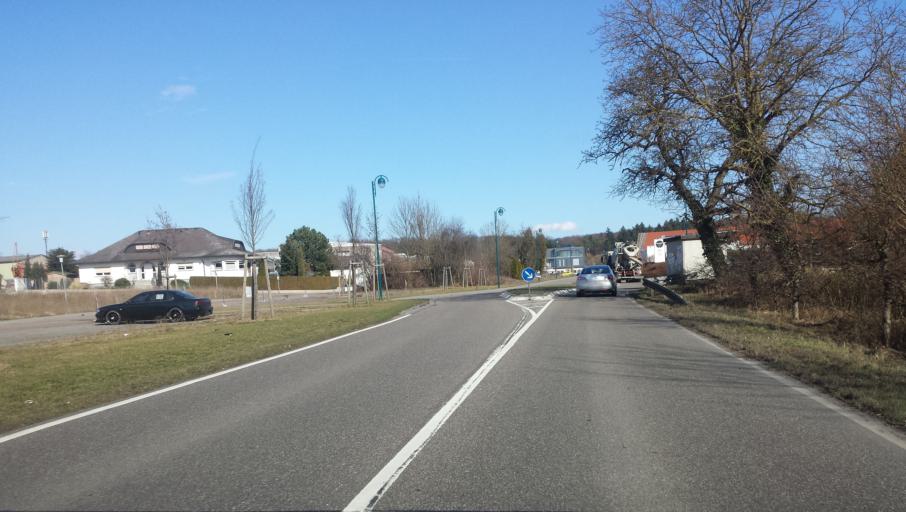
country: DE
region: Baden-Wuerttemberg
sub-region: Karlsruhe Region
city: Ostringen
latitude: 49.2237
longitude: 8.7229
